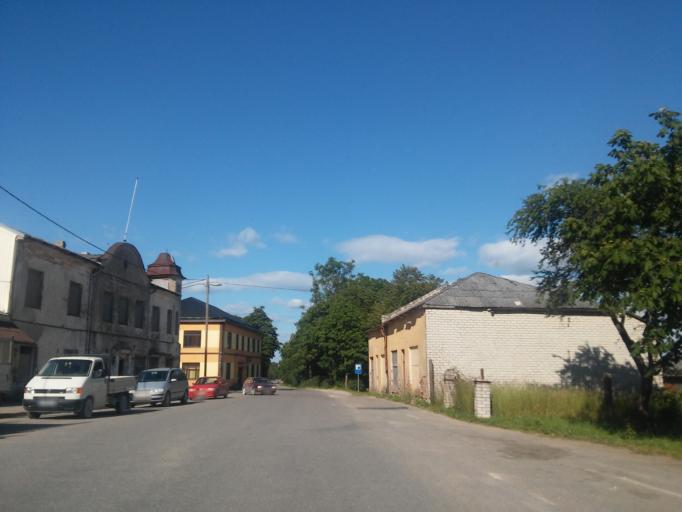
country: LV
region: Vainode
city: Vainode
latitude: 56.4166
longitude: 21.8546
